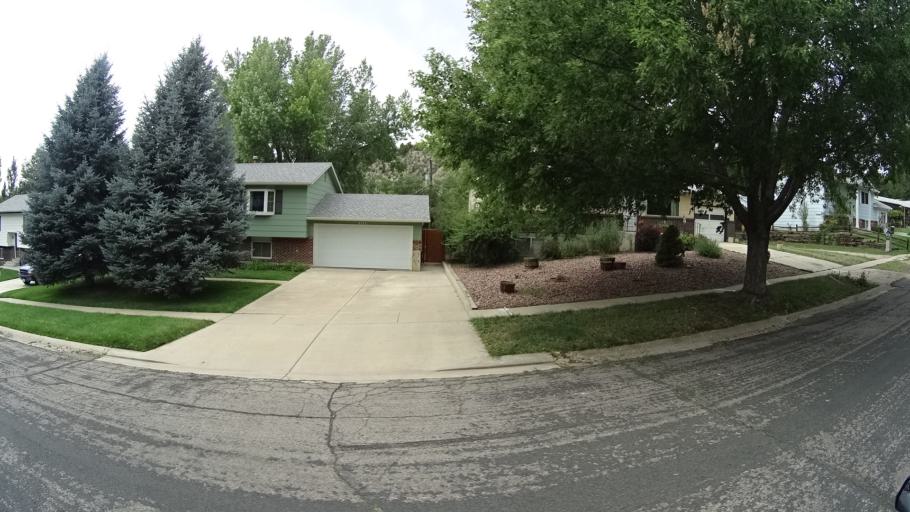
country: US
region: Colorado
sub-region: El Paso County
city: Manitou Springs
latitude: 38.8615
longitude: -104.8714
